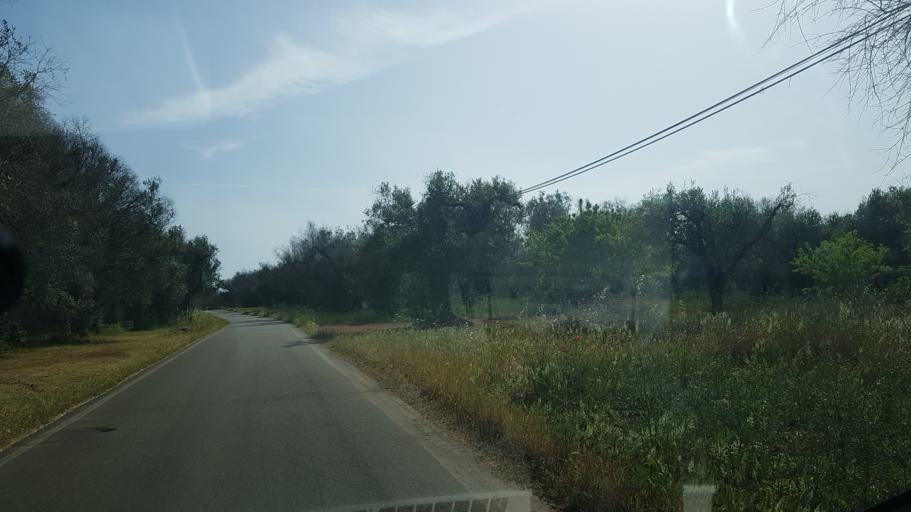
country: IT
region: Apulia
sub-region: Provincia di Brindisi
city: Torchiarolo
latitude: 40.5078
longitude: 18.0699
